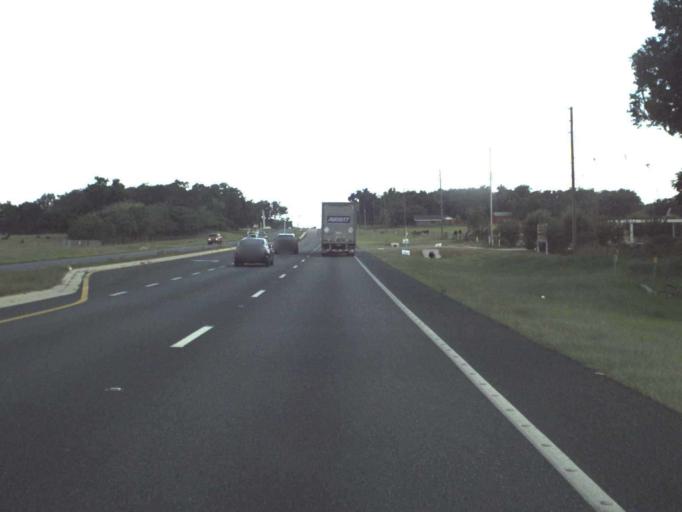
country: US
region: Florida
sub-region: Sumter County
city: Wildwood
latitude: 28.9069
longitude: -82.0372
